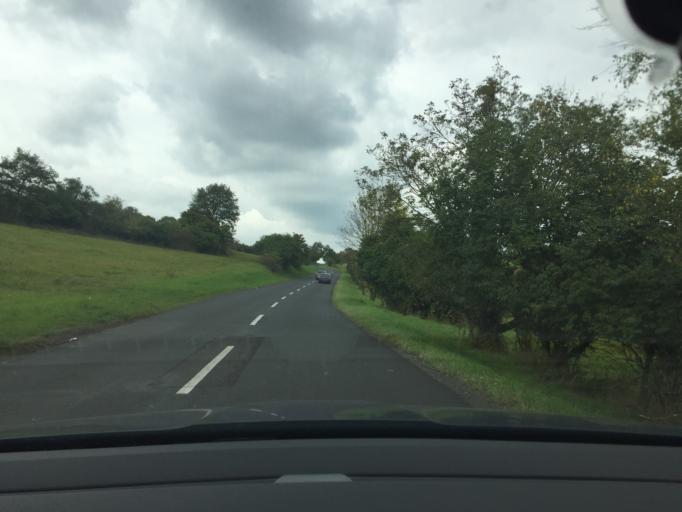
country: CZ
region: Ustecky
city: Lovosice
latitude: 50.5533
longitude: 14.0717
